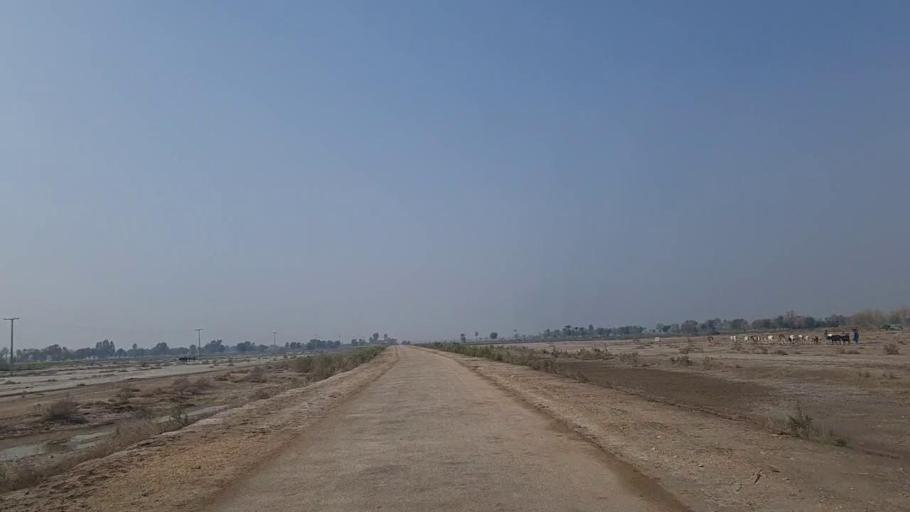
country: PK
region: Sindh
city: Nawabshah
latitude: 26.3600
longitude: 68.4296
